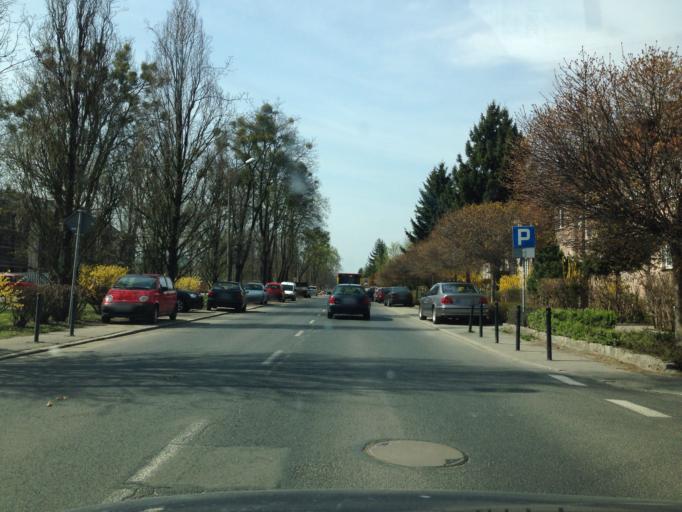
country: PL
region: Lower Silesian Voivodeship
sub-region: Powiat wroclawski
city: Radwanice
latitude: 51.1065
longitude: 17.1024
